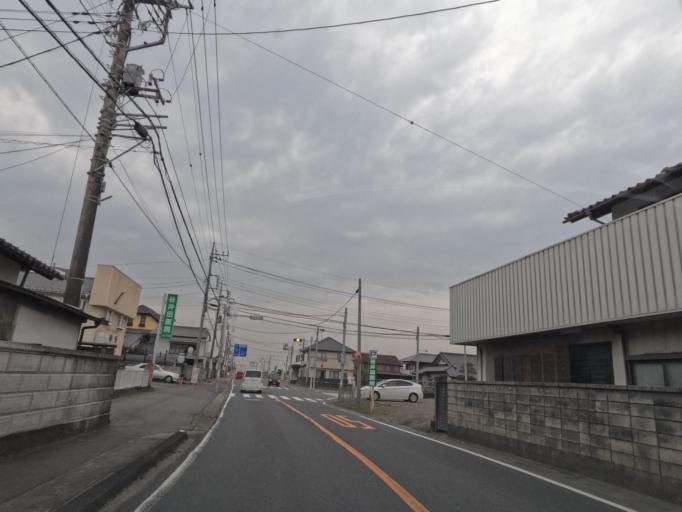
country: JP
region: Ibaraki
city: Moriya
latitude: 35.9589
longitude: 140.0469
